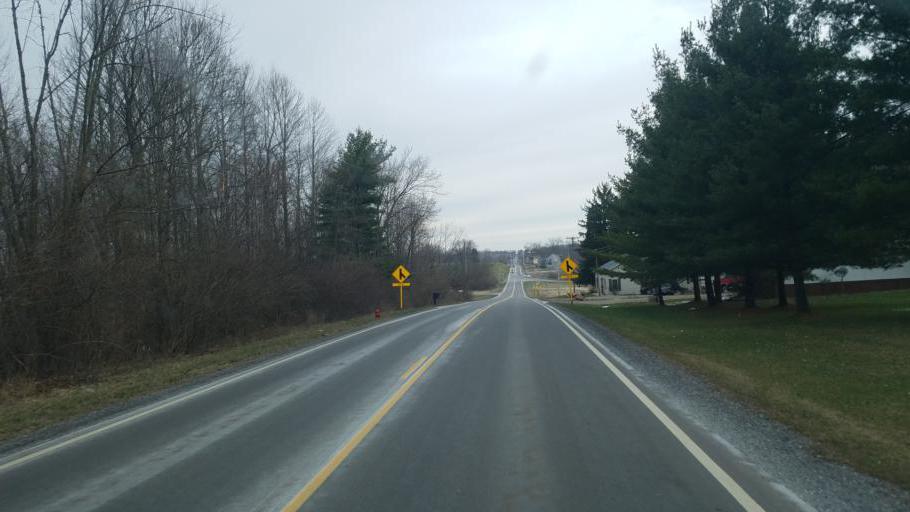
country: US
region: Ohio
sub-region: Morrow County
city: Mount Gilead
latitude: 40.5354
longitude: -82.8318
